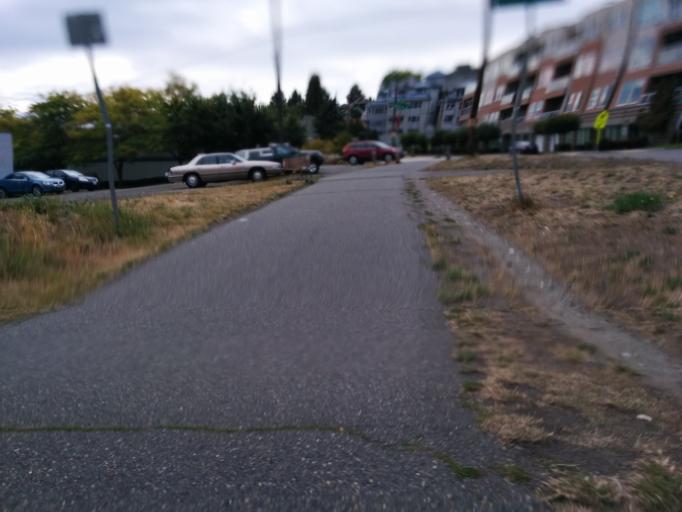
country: US
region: Washington
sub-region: King County
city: Seattle
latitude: 47.6549
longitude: -122.3250
